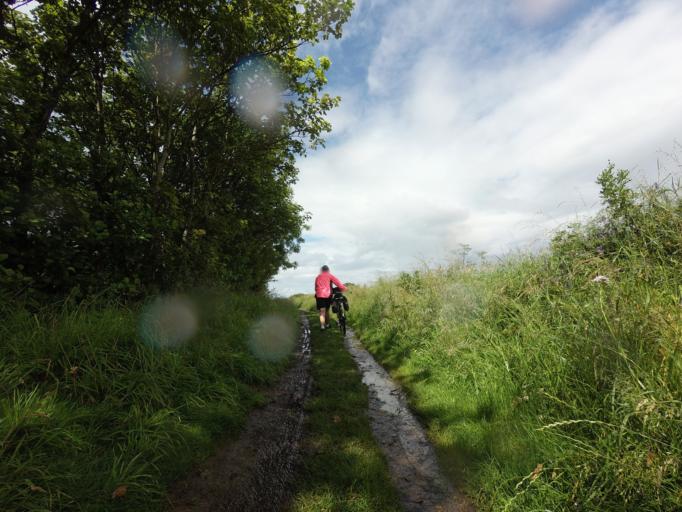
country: GB
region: Scotland
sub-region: Moray
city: Fochabers
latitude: 57.6706
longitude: -3.0917
